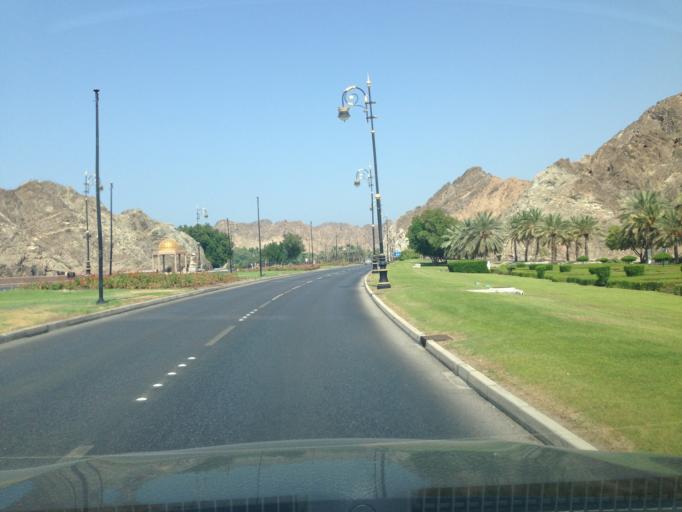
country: OM
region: Muhafazat Masqat
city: Muscat
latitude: 23.6223
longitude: 58.5704
